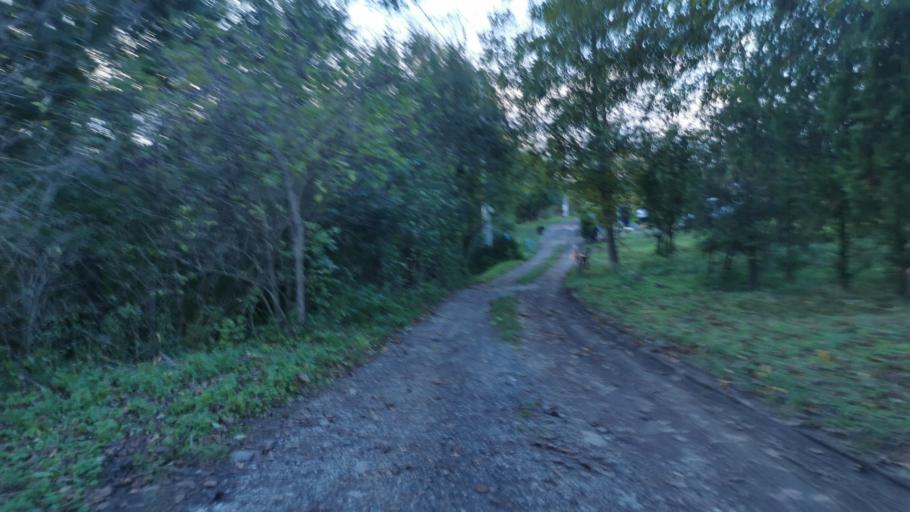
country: SK
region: Trnavsky
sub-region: Okres Skalica
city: Skalica
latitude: 48.8214
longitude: 17.2325
